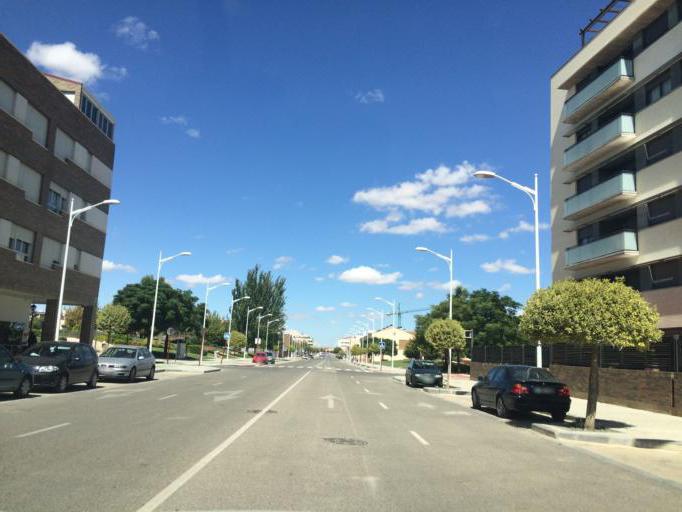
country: ES
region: Castille-La Mancha
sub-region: Provincia de Albacete
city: Albacete
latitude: 38.9779
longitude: -1.8410
